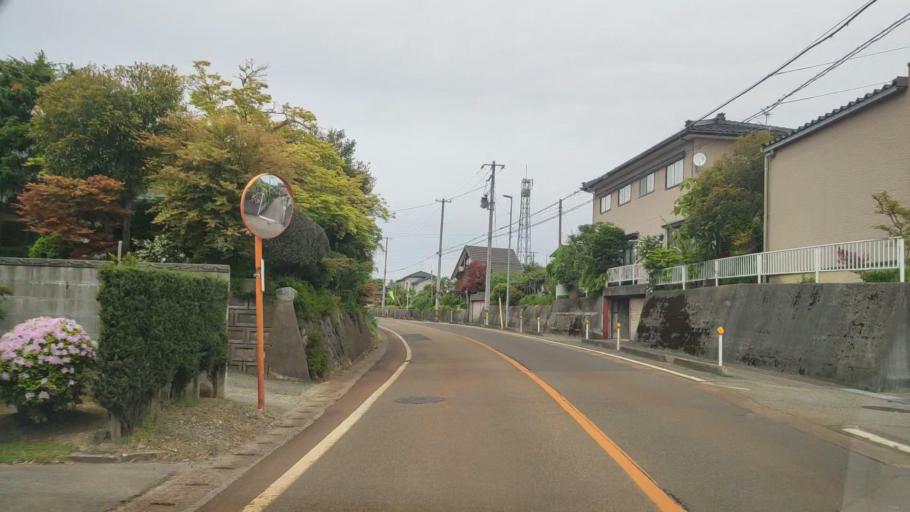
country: JP
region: Niigata
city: Shirone
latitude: 37.7262
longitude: 139.0803
